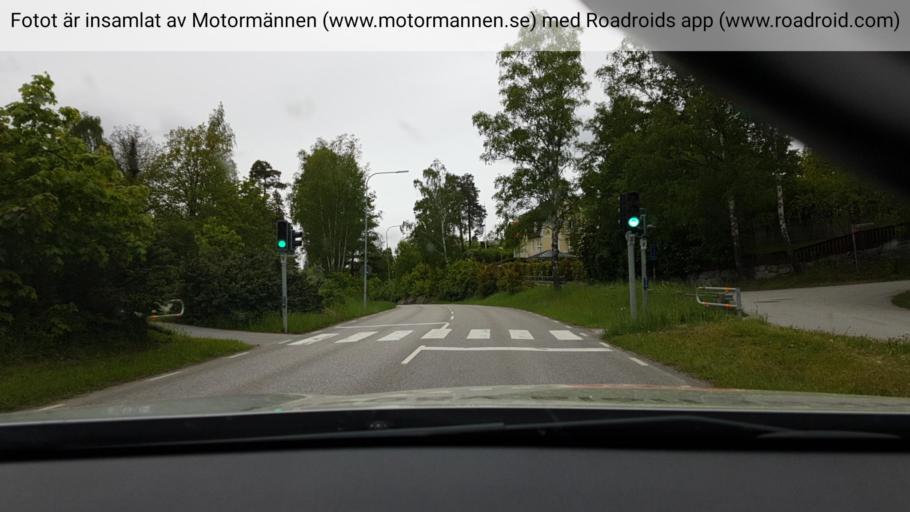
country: SE
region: Stockholm
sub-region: Lidingo
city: Lidingoe
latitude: 59.3680
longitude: 18.1330
